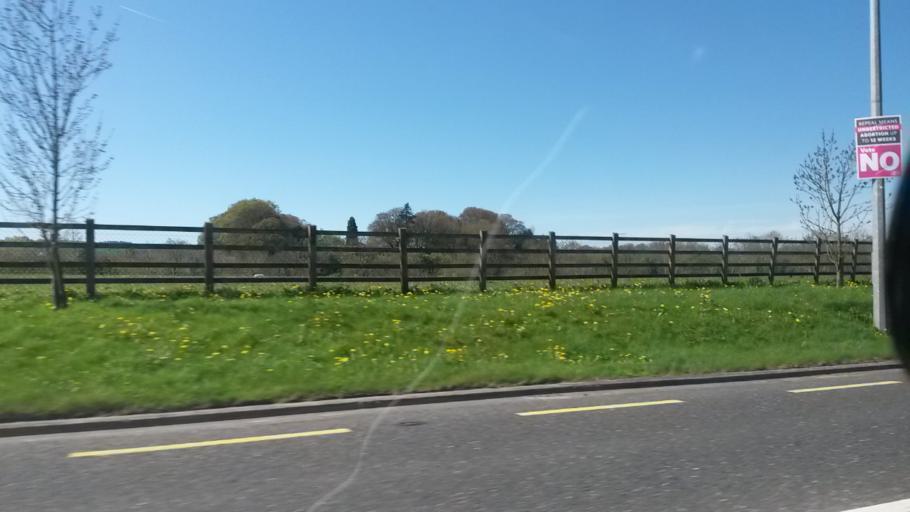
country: IE
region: Munster
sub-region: County Cork
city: Killumney
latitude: 51.8795
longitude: -8.6505
